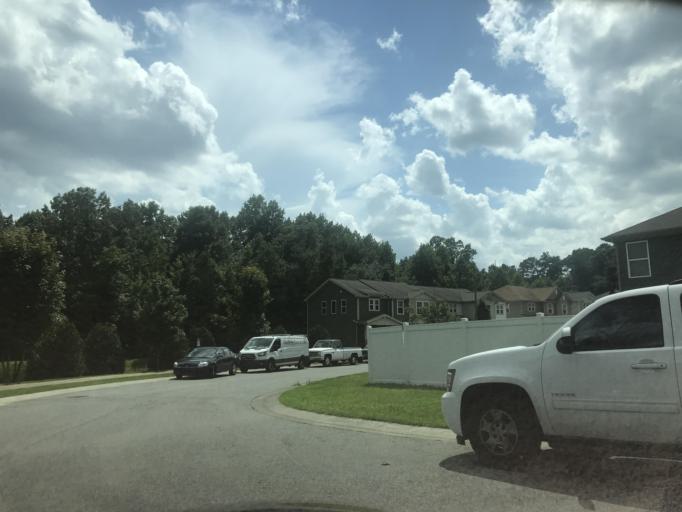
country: US
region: North Carolina
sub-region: Wake County
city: Knightdale
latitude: 35.8536
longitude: -78.5601
